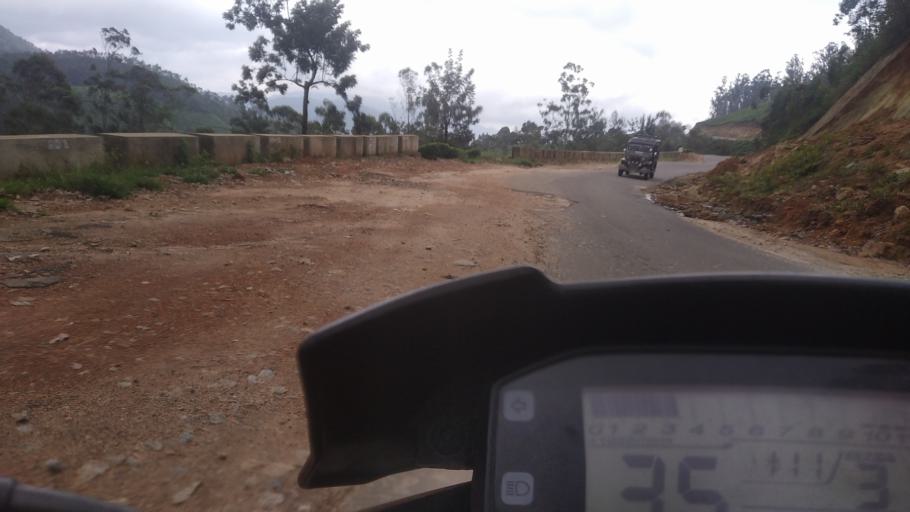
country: IN
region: Kerala
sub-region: Idukki
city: Munnar
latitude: 10.0824
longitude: 77.0741
